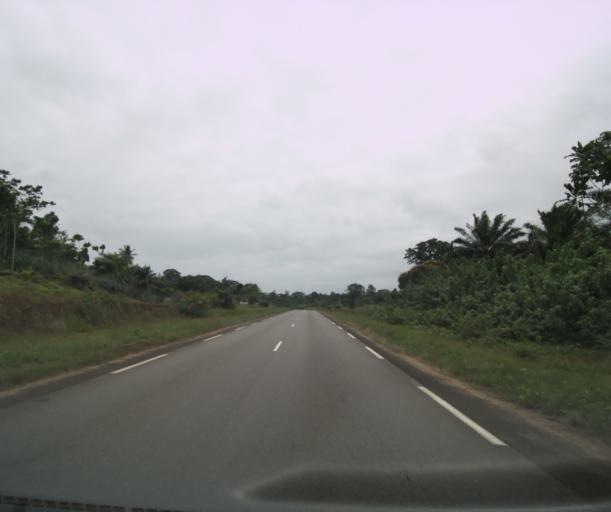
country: CM
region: South Province
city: Kribi
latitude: 3.1384
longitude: 10.0114
